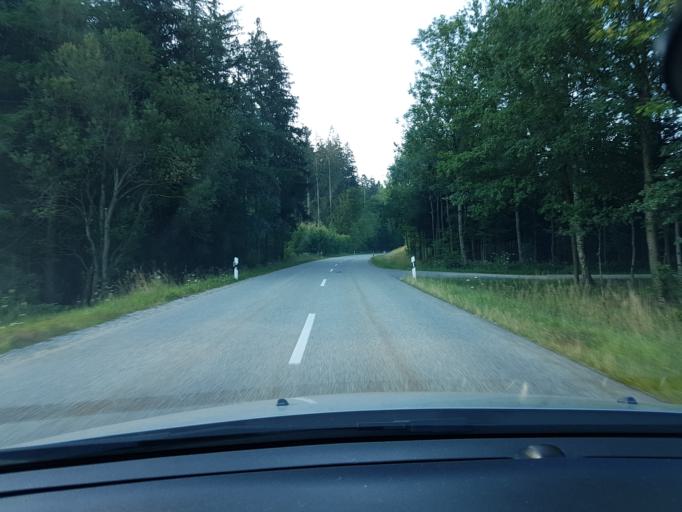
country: DE
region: Bavaria
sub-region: Lower Bavaria
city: Schalkham
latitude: 48.4581
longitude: 12.4733
